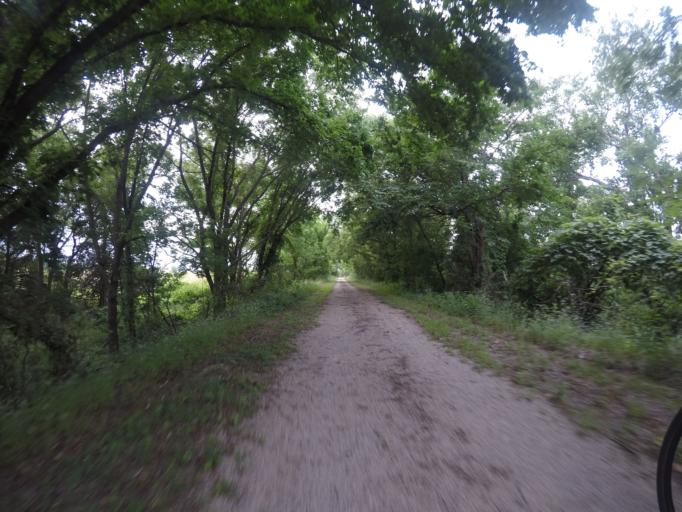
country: US
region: Kansas
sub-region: Franklin County
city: Ottawa
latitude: 38.4776
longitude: -95.2748
